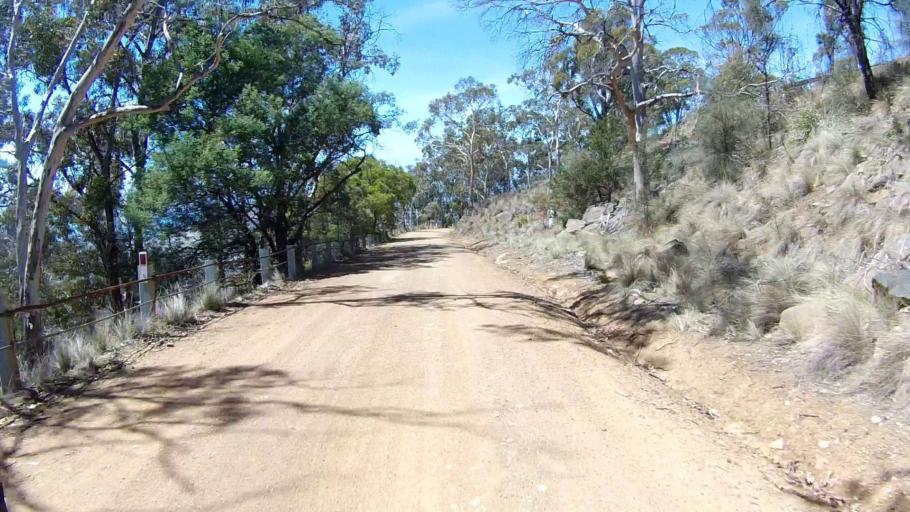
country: AU
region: Tasmania
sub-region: Clarence
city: Cambridge
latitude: -42.8604
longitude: 147.4544
